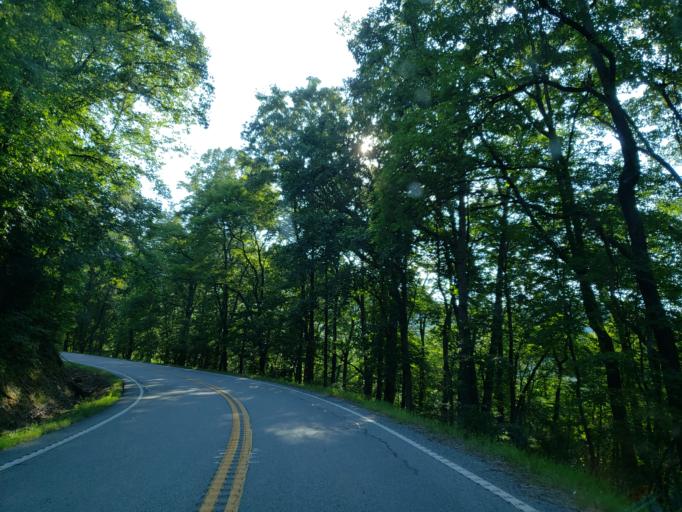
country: US
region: Georgia
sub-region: Fannin County
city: Blue Ridge
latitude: 34.8110
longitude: -84.1865
